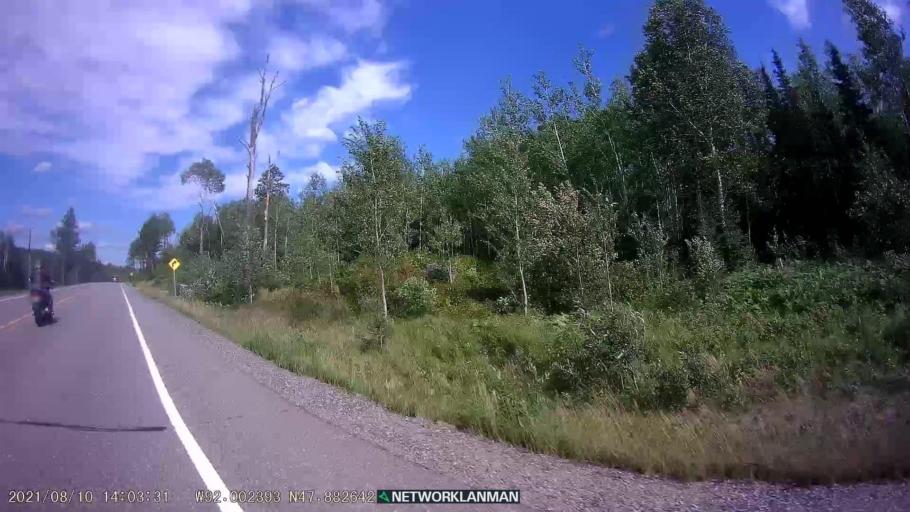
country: US
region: Minnesota
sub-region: Saint Louis County
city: Ely
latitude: 47.8828
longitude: -92.0021
